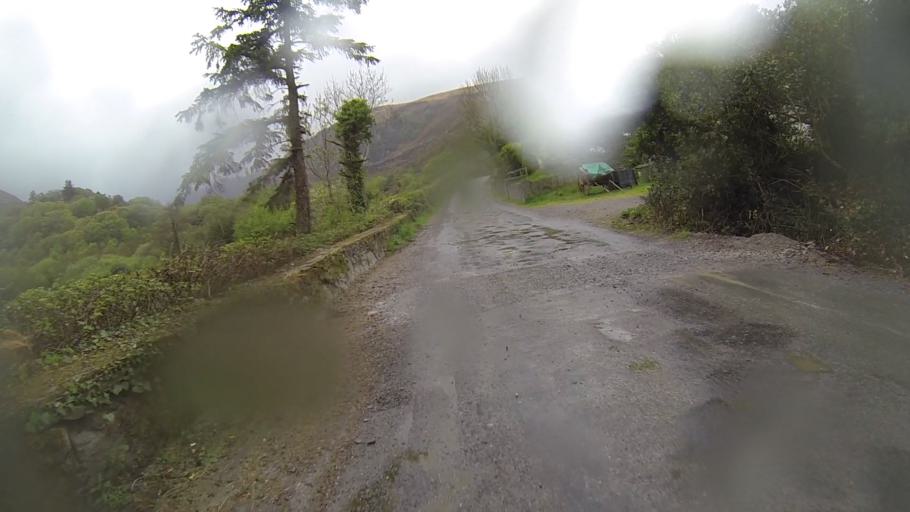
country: IE
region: Munster
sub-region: Ciarrai
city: Cill Airne
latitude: 52.0394
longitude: -9.6328
